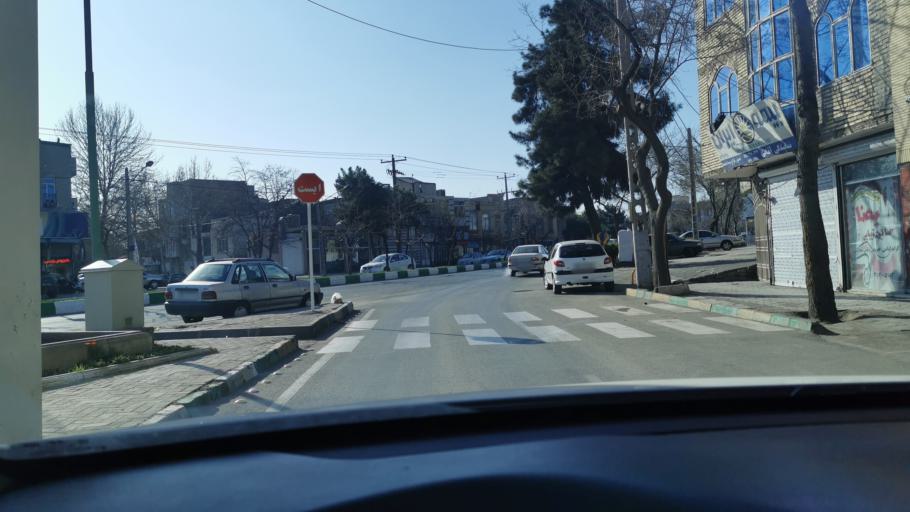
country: IR
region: Razavi Khorasan
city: Mashhad
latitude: 36.2757
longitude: 59.5761
